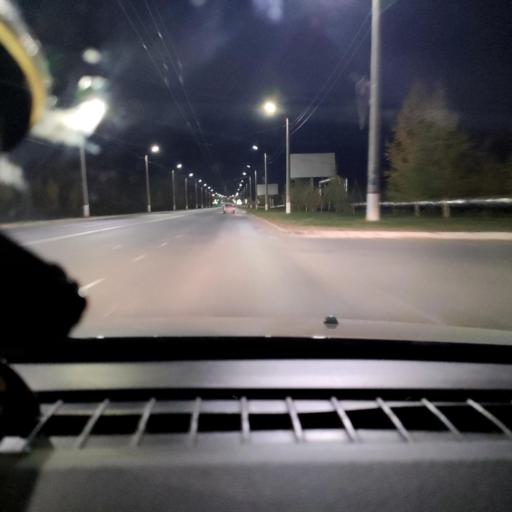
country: RU
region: Samara
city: Novokuybyshevsk
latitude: 53.1004
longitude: 49.9392
